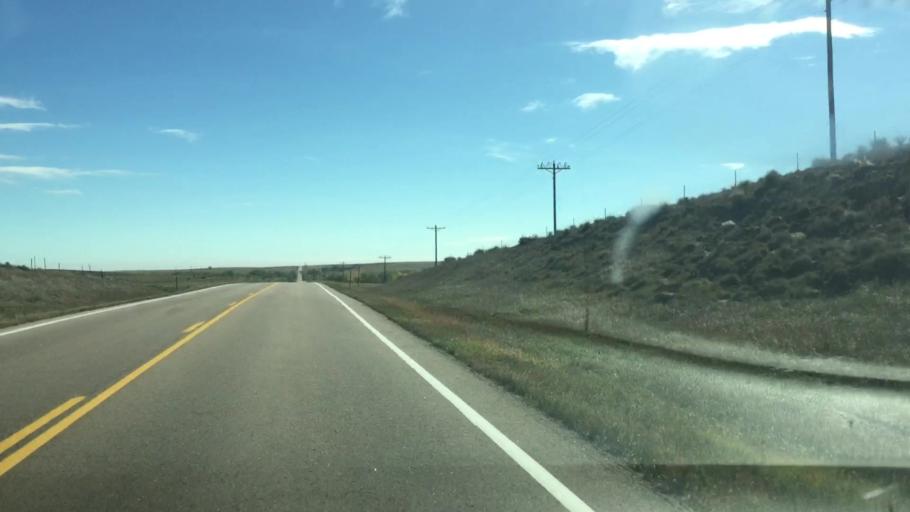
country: US
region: Colorado
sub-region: Elbert County
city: Kiowa
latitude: 39.2736
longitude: -104.1544
